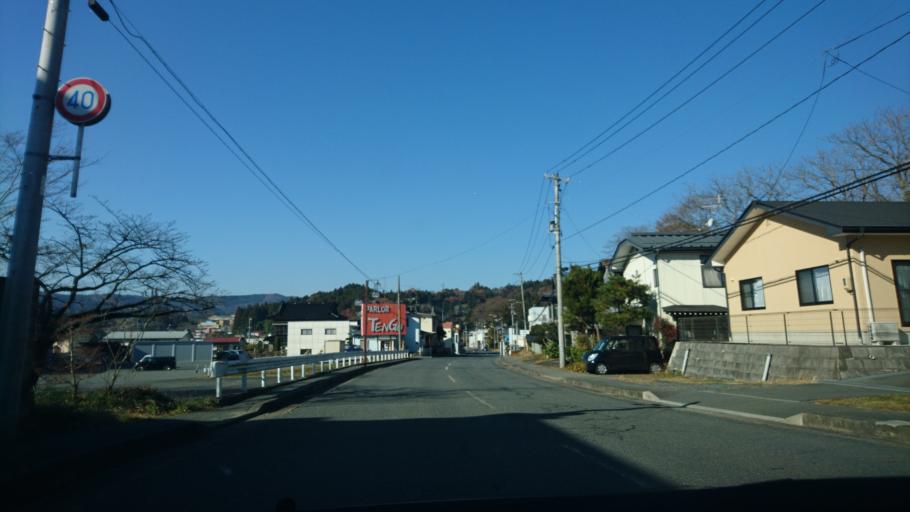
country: JP
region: Iwate
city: Ichinoseki
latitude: 38.9180
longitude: 141.3400
